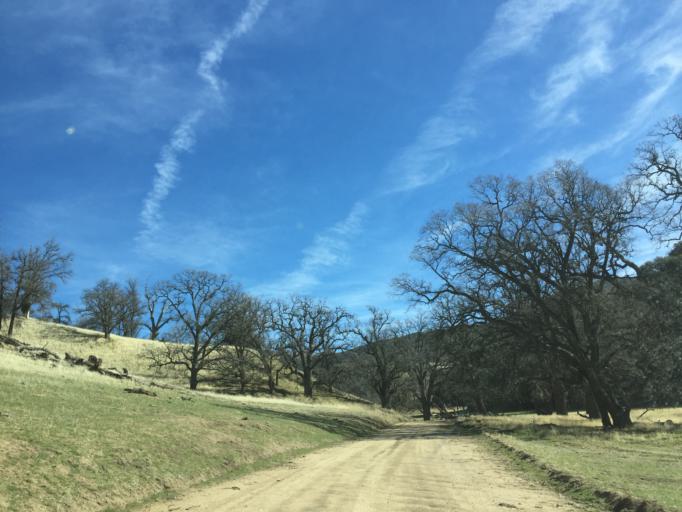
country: US
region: California
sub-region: Kern County
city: Stallion Springs
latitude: 34.9146
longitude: -118.6892
